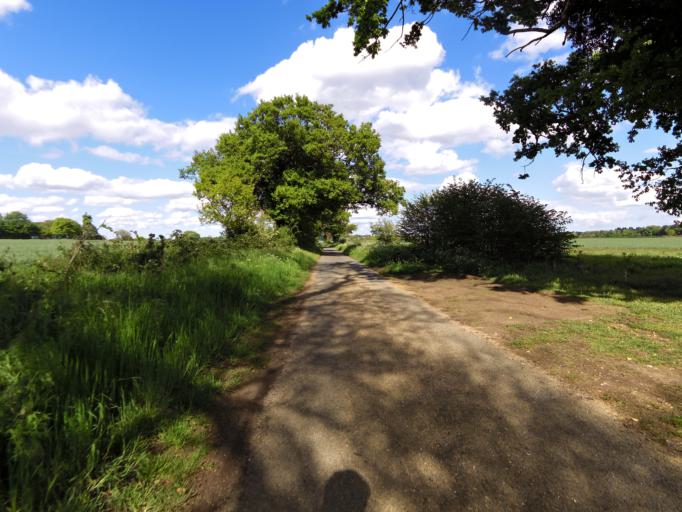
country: GB
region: England
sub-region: Suffolk
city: Thurston
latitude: 52.2487
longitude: 0.7883
